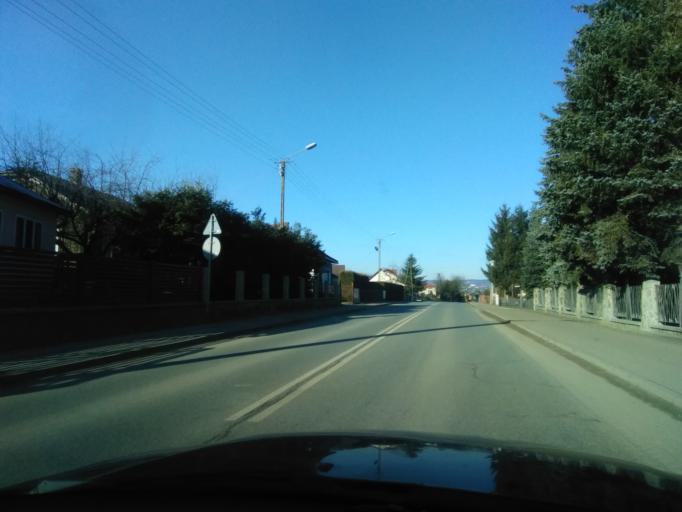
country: PL
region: Subcarpathian Voivodeship
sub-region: Powiat brzozowski
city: Haczow
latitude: 49.6701
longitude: 21.8888
